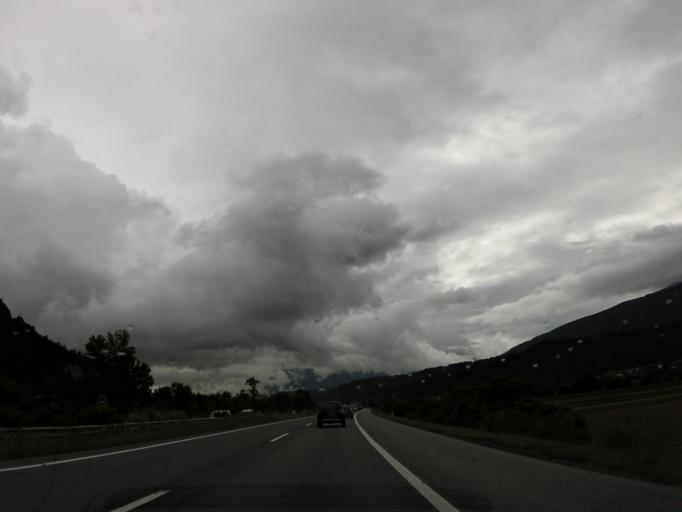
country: AT
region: Tyrol
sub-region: Politischer Bezirk Innsbruck Land
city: Kematen in Tirol
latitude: 47.2654
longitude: 11.2828
